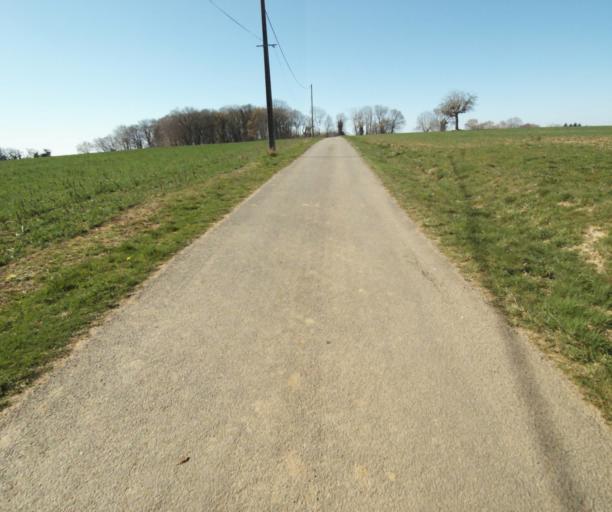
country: FR
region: Limousin
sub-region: Departement de la Correze
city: Chamboulive
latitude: 45.4104
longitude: 1.6475
